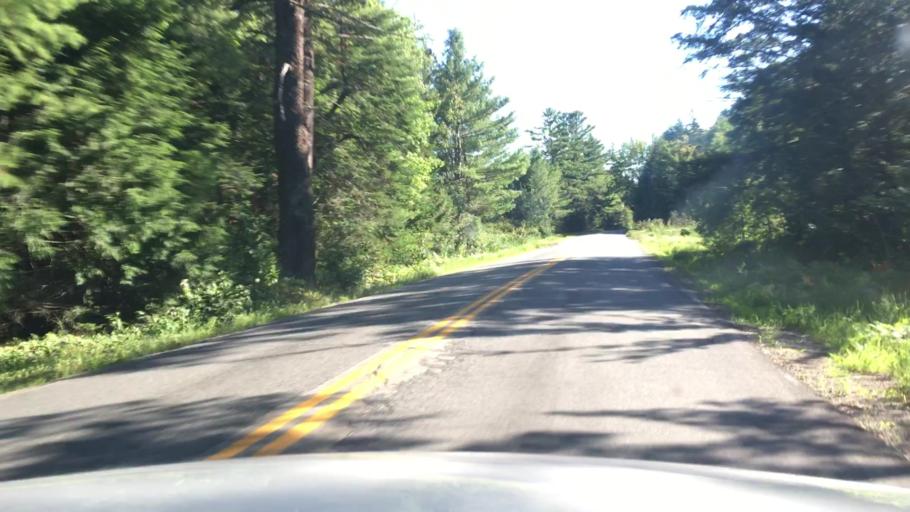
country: US
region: Maine
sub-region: Penobscot County
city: Enfield
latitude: 45.2080
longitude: -68.5920
